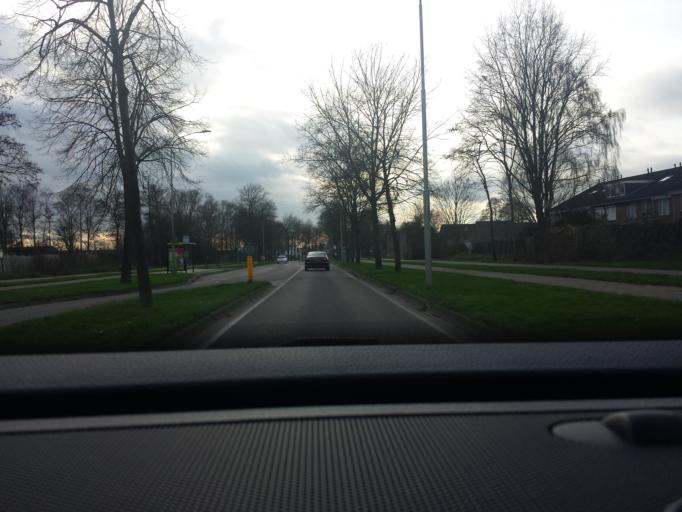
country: NL
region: Gelderland
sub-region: Gemeente Duiven
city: Duiven
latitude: 51.9444
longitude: 6.0260
